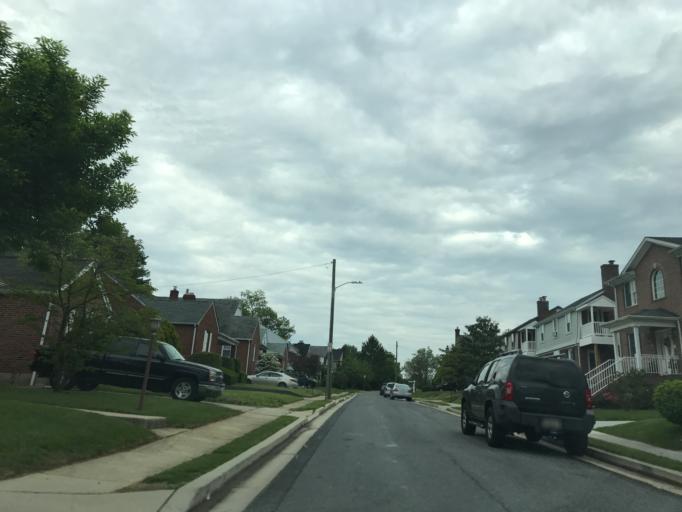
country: US
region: Maryland
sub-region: Baltimore County
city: Parkville
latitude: 39.3783
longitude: -76.5441
